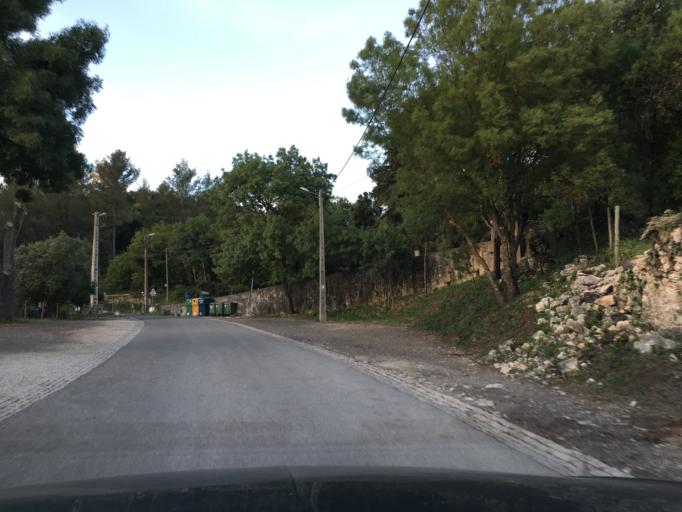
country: PT
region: Lisbon
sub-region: Oeiras
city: Barcarena
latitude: 38.7260
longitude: -9.2769
